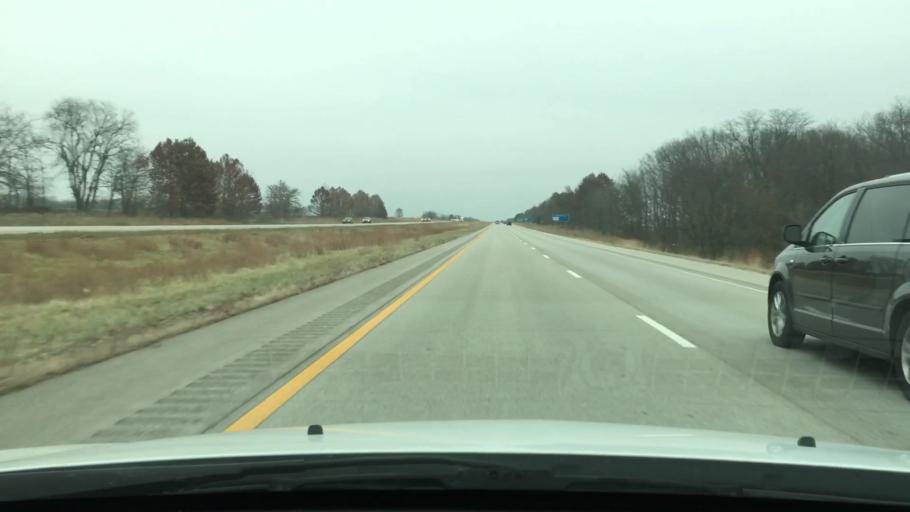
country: US
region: Illinois
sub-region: Sangamon County
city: New Berlin
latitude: 39.7398
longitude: -89.9579
